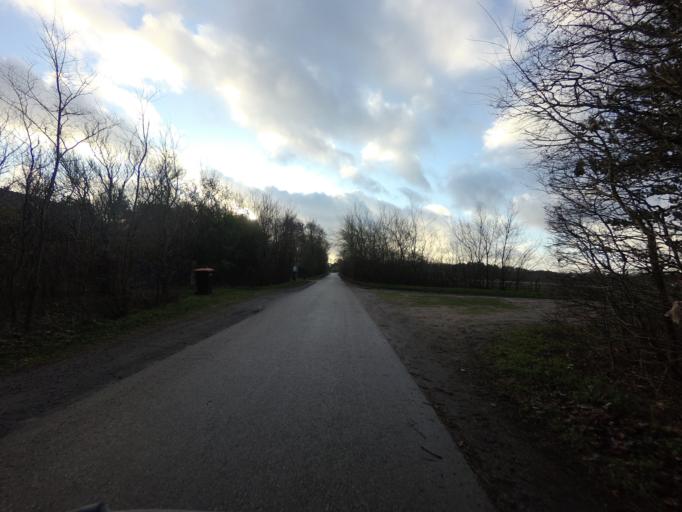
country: NL
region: North Holland
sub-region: Gemeente Texel
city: Den Burg
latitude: 53.0953
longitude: 4.7729
